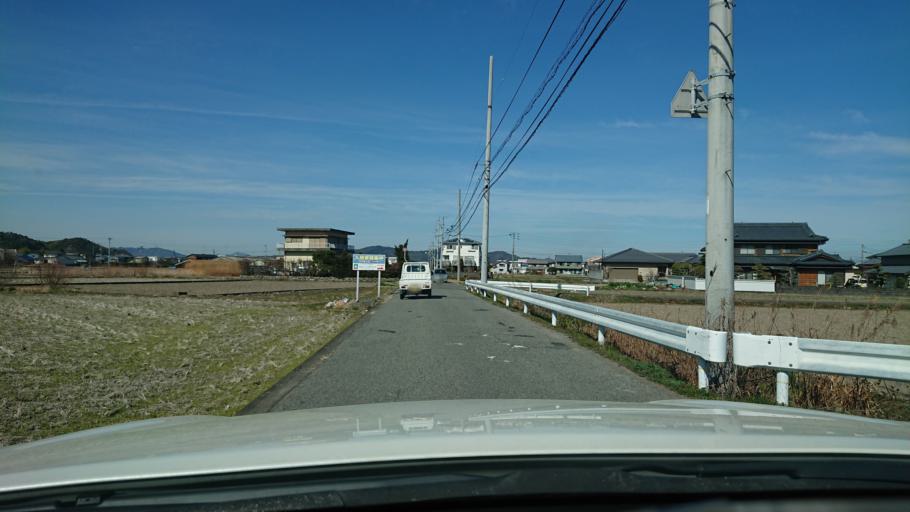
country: JP
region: Tokushima
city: Komatsushimacho
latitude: 33.9805
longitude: 134.5884
